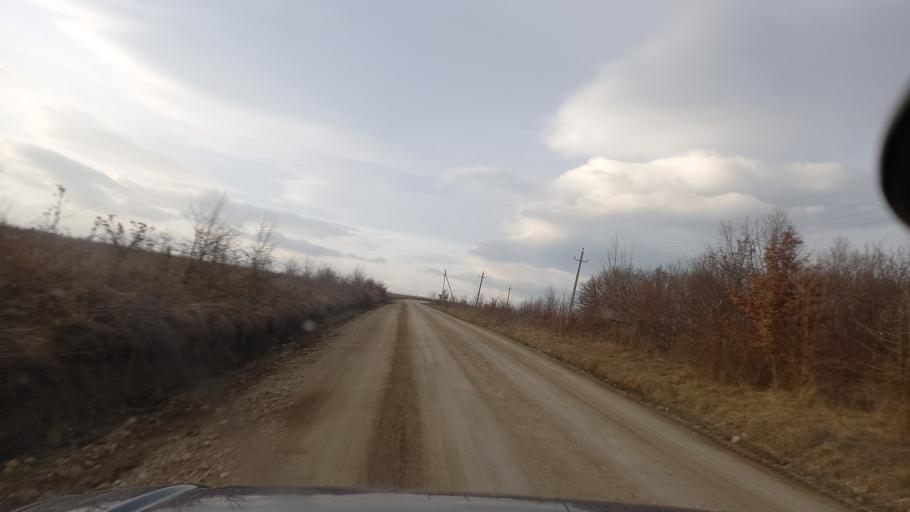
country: RU
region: Adygeya
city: Kamennomostskiy
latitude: 44.1951
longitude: 40.2544
